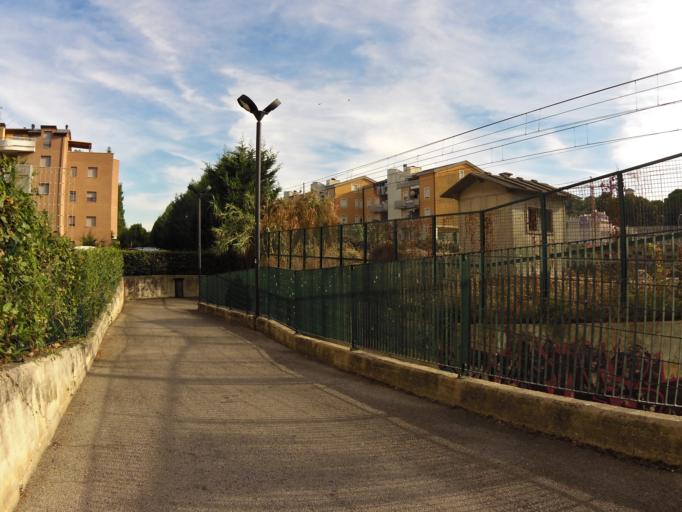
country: IT
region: The Marches
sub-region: Provincia di Macerata
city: Porto Recanati
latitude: 43.4263
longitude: 13.6642
